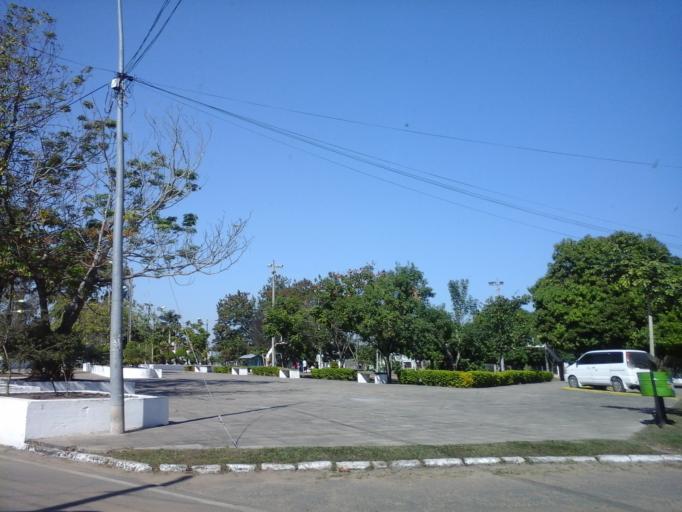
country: PY
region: Neembucu
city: Pilar
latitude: -26.8579
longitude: -58.3089
